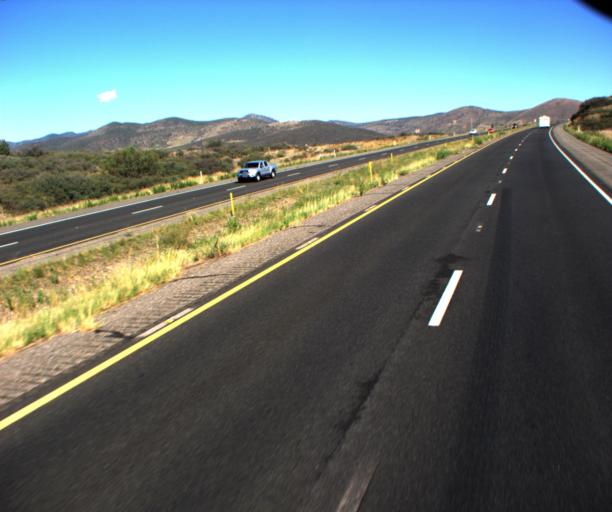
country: US
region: Arizona
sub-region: Yavapai County
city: Mayer
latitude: 34.4324
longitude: -112.2583
